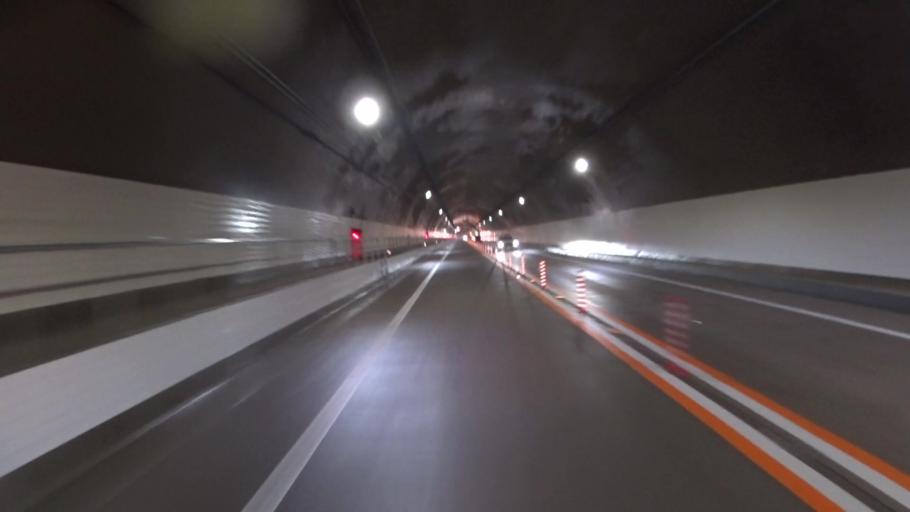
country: JP
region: Kyoto
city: Ayabe
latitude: 35.2482
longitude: 135.3422
